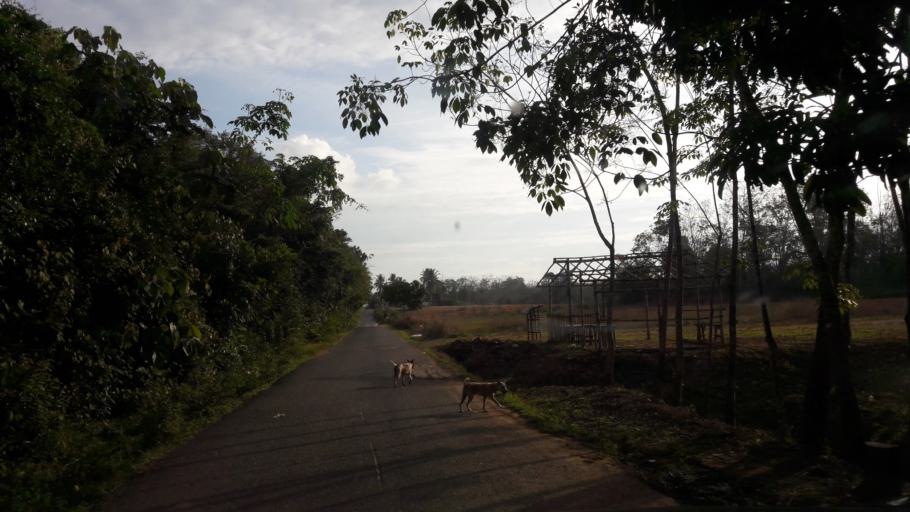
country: ID
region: South Sumatra
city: Gunungmegang Dalam
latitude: -3.2440
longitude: 103.8339
